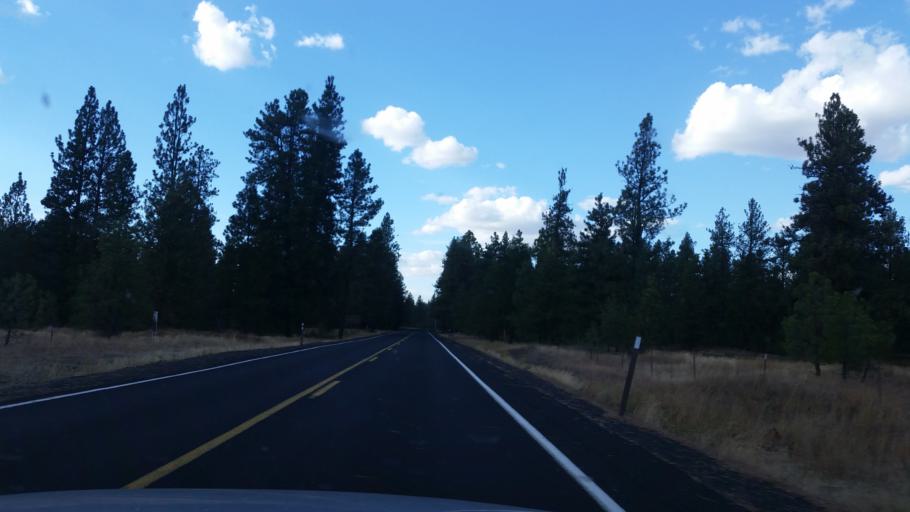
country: US
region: Washington
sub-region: Spokane County
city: Cheney
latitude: 47.4544
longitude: -117.5773
